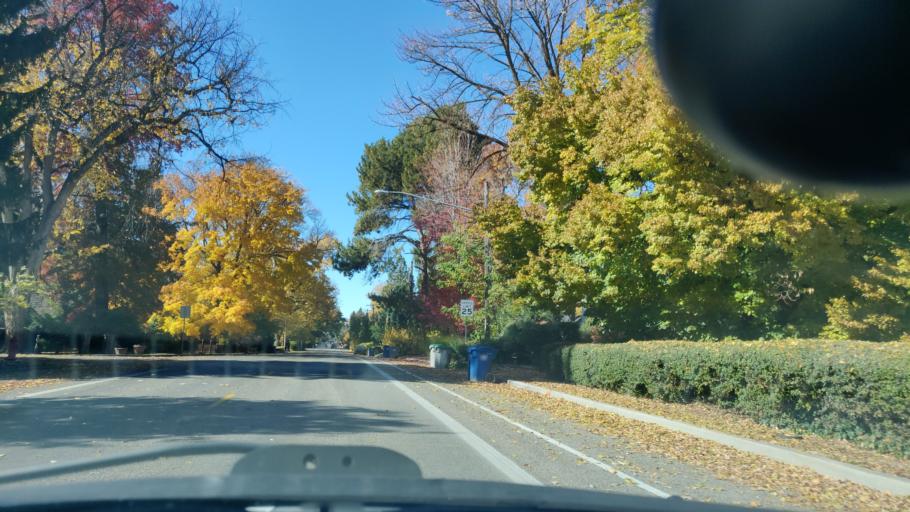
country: US
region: Idaho
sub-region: Ada County
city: Boise
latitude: 43.5935
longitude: -116.2207
